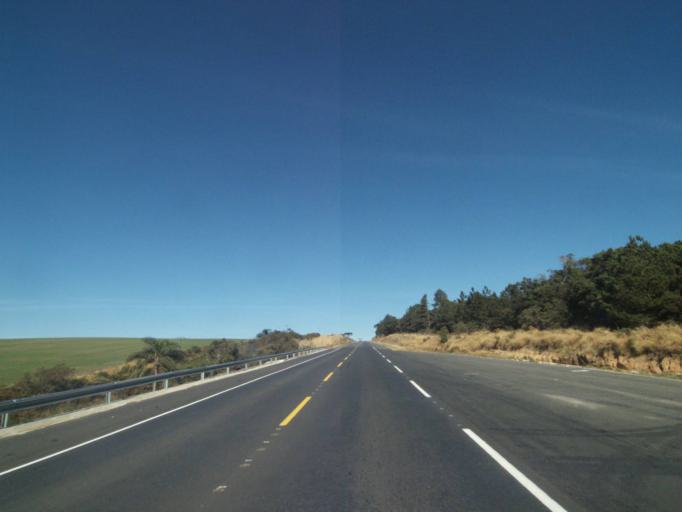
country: BR
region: Parana
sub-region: Tibagi
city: Tibagi
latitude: -24.7941
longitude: -50.4663
